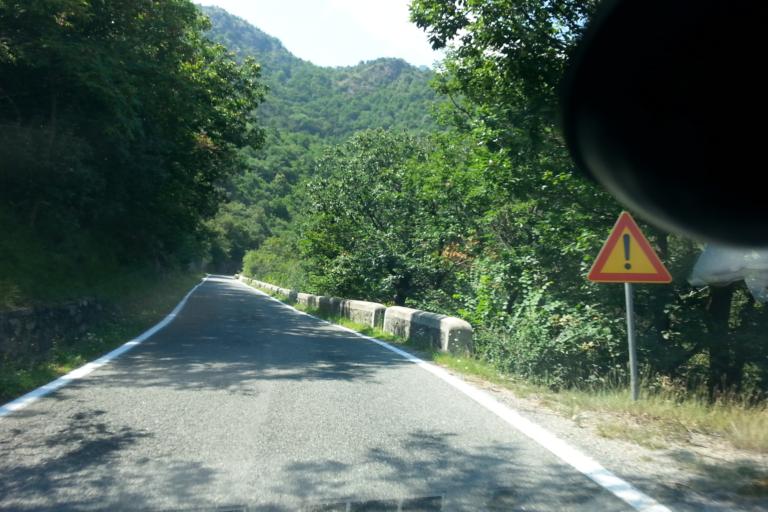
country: IT
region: Piedmont
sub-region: Provincia di Torino
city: Sant'Ambrogio di Torino
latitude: 45.0873
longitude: 7.3578
